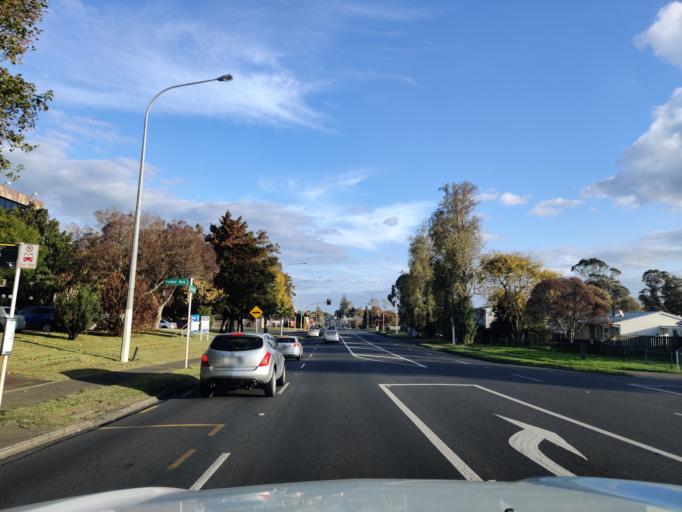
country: NZ
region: Auckland
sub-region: Auckland
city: Manukau City
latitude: -36.9529
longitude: 174.8912
